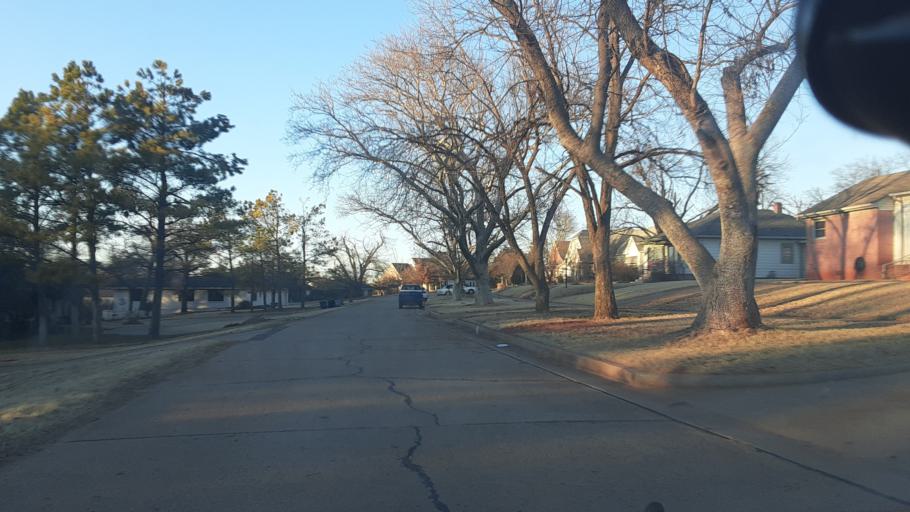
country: US
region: Oklahoma
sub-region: Logan County
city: Guthrie
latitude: 35.8824
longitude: -97.4143
